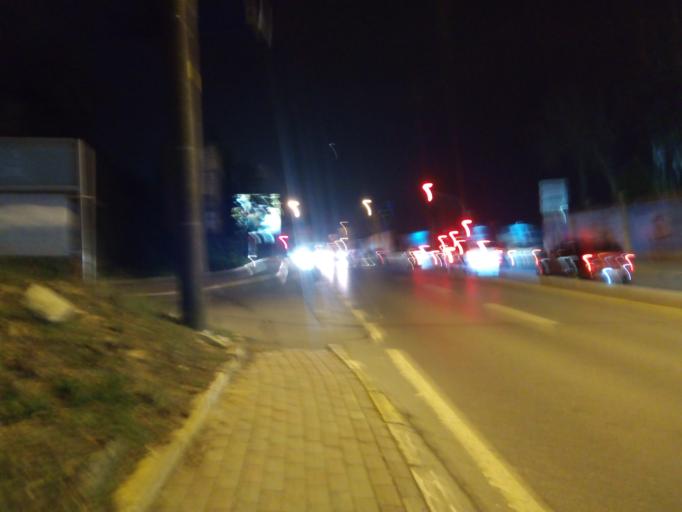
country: TR
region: Istanbul
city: Sisli
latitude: 41.1120
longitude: 29.0408
